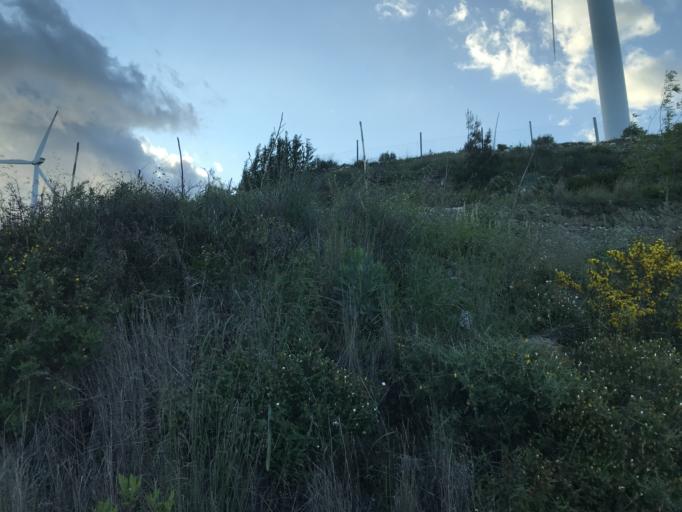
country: TR
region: Hatay
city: Buyukcat
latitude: 36.1088
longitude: 36.0482
